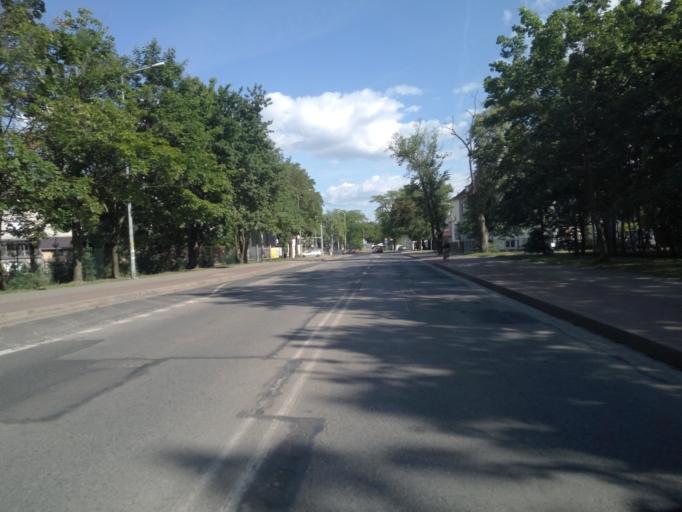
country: PL
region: Lower Silesian Voivodeship
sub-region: Powiat wroclawski
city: Wroclaw
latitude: 51.1419
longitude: 16.9565
